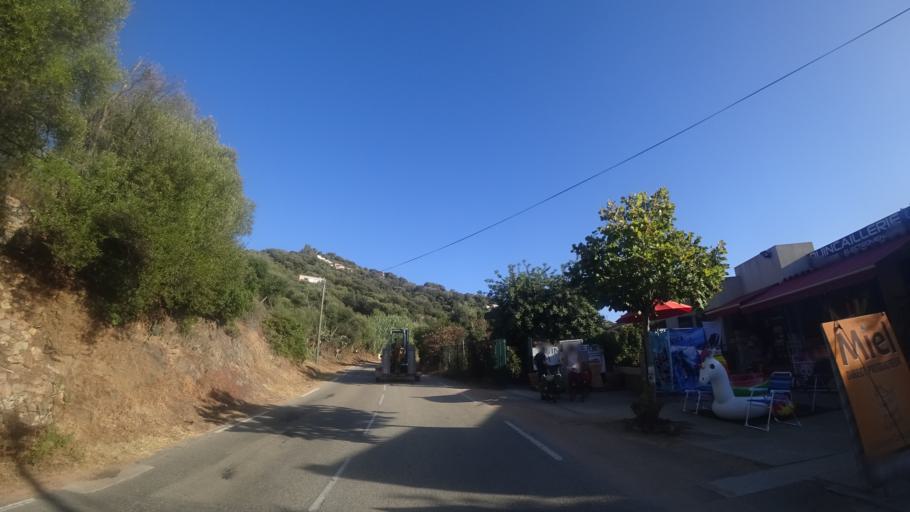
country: FR
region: Corsica
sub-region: Departement de la Corse-du-Sud
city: Cargese
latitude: 42.1444
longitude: 8.6026
